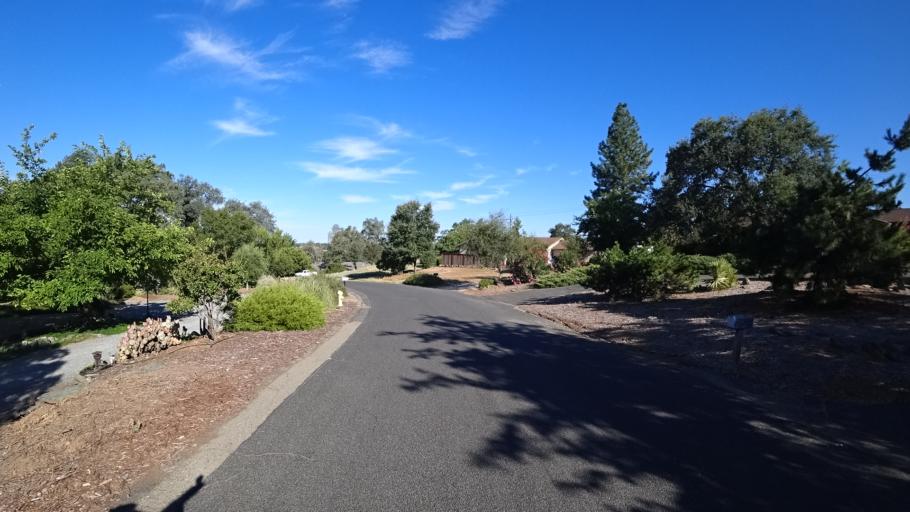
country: US
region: California
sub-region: Calaveras County
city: San Andreas
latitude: 38.1881
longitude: -120.6584
